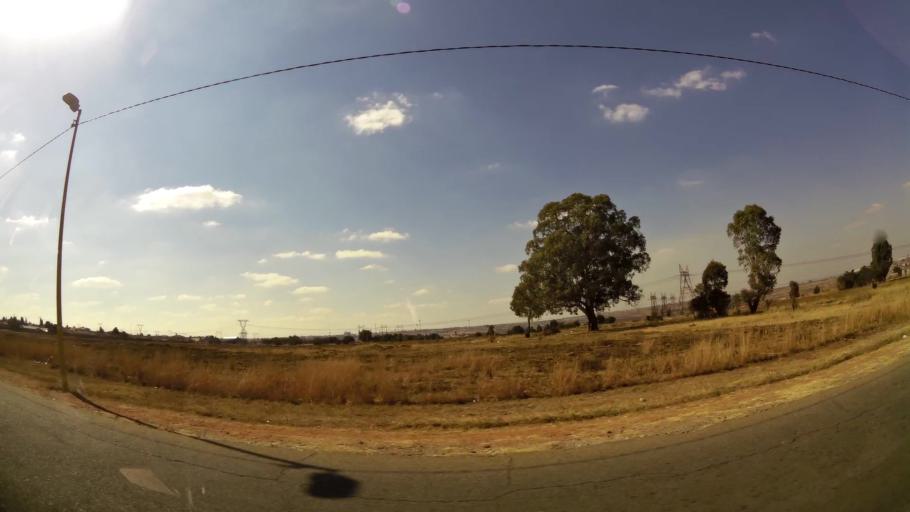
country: ZA
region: Gauteng
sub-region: West Rand District Municipality
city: Randfontein
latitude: -26.1803
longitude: 27.7492
